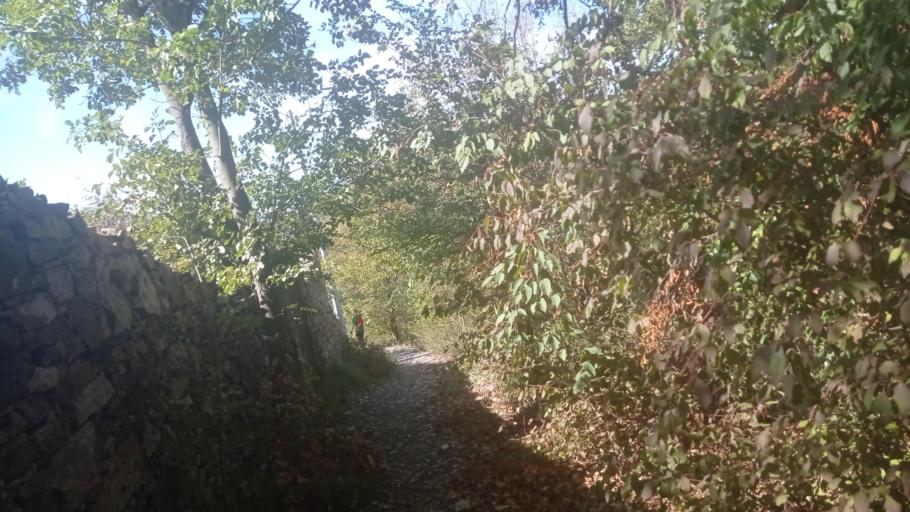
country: IT
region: Liguria
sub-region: Provincia di Genova
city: Genoa
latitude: 44.4111
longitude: 8.9839
